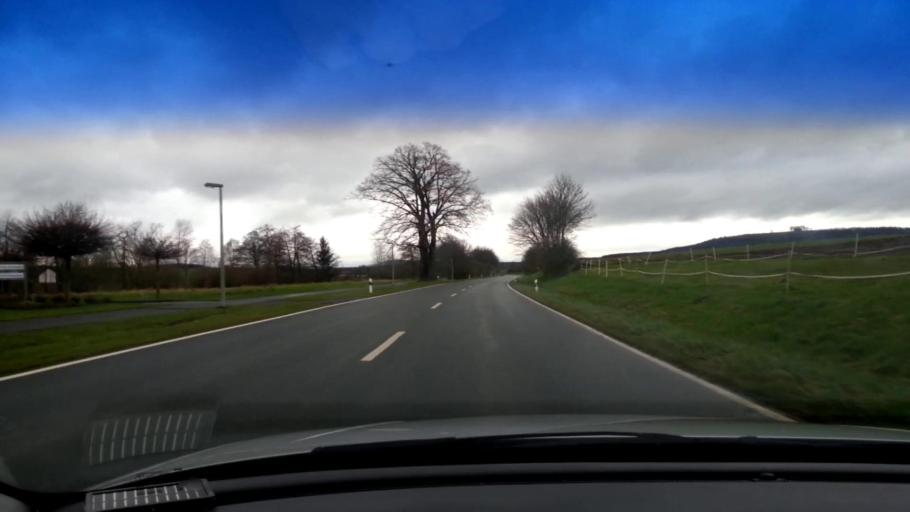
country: DE
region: Bavaria
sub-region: Upper Franconia
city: Ebensfeld
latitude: 50.0370
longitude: 11.0018
